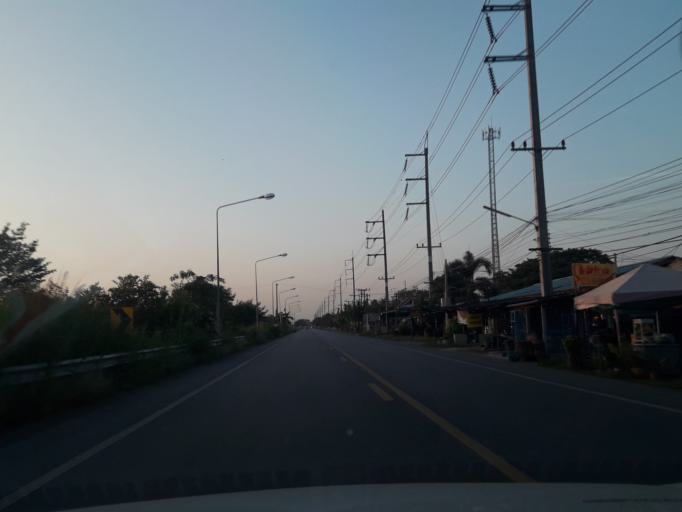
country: TH
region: Phra Nakhon Si Ayutthaya
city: Bang Pahan
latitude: 14.4924
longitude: 100.5555
